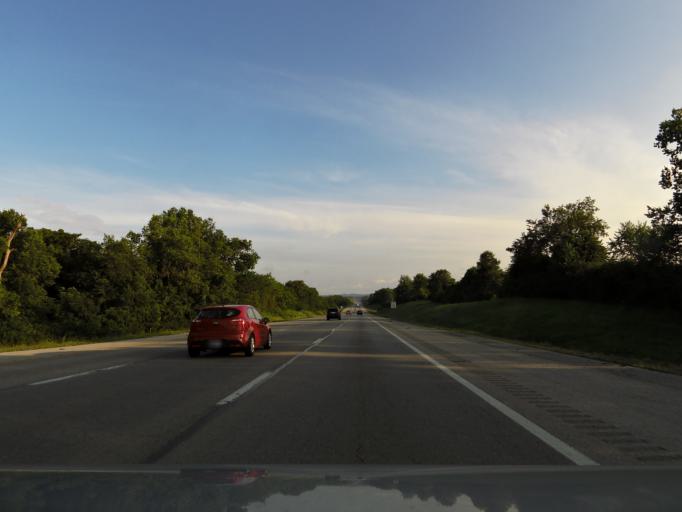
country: US
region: Kentucky
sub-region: Madison County
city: Richmond
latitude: 37.6644
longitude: -84.3116
